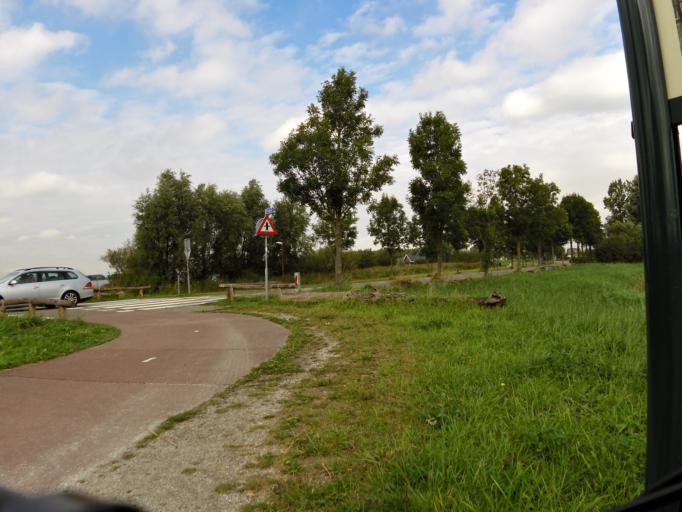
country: NL
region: South Holland
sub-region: Gemeente Rijnwoude
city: Benthuizen
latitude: 52.0820
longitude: 4.5179
